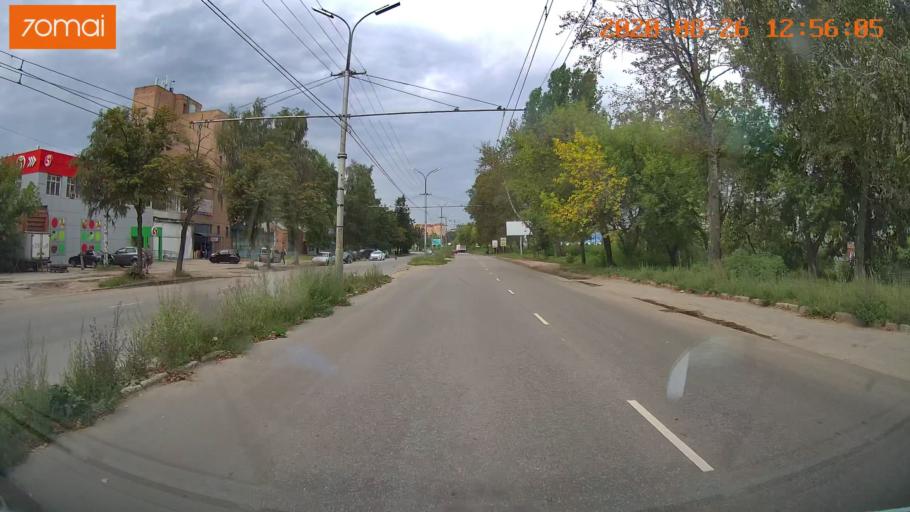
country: RU
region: Rjazan
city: Ryazan'
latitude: 54.6120
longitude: 39.7539
